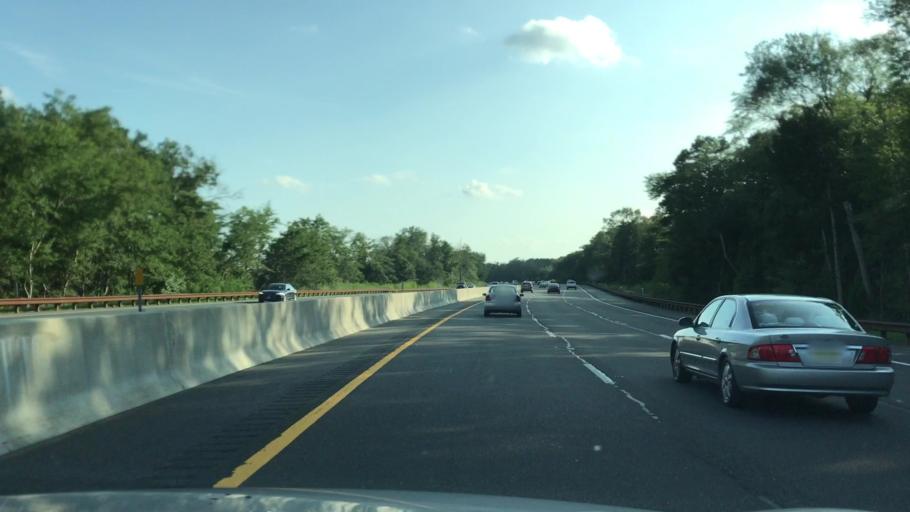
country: US
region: New Jersey
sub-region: Atlantic County
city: Port Republic
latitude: 39.5866
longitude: -74.4510
